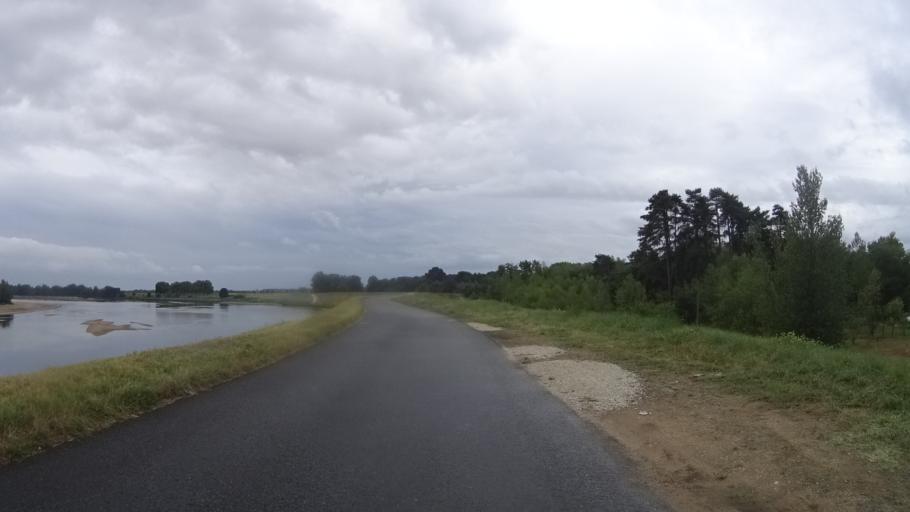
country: FR
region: Centre
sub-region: Departement du Loiret
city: Sandillon
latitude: 47.8578
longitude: 2.0310
